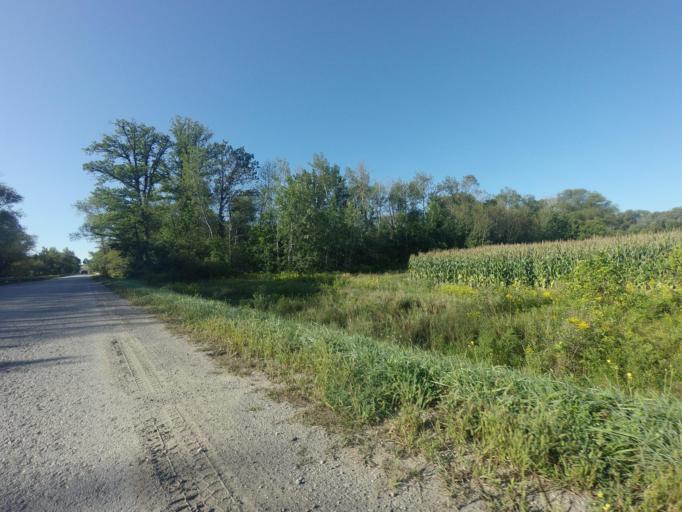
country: CA
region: Ontario
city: Bradford West Gwillimbury
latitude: 44.0595
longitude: -79.6294
